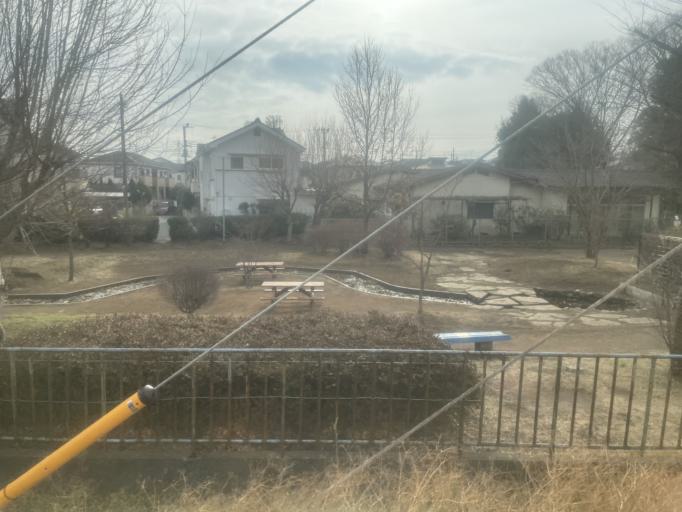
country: JP
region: Tokyo
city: Higashimurayama-shi
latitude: 35.7720
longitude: 139.4716
